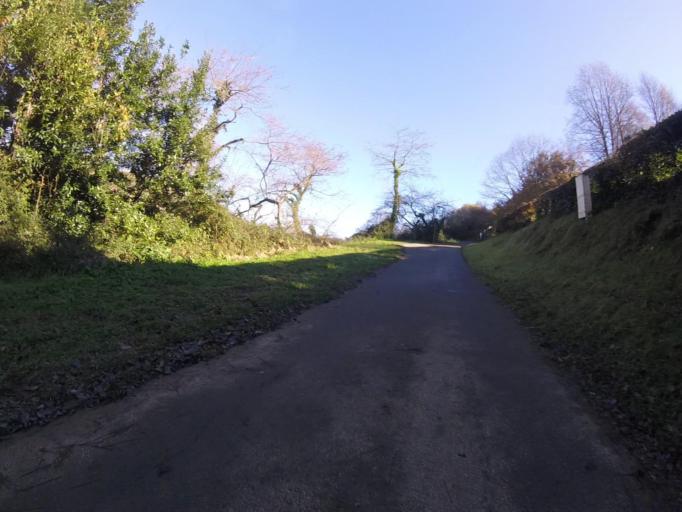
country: FR
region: Aquitaine
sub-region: Departement des Pyrenees-Atlantiques
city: Urrugne
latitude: 43.3325
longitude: -1.7383
